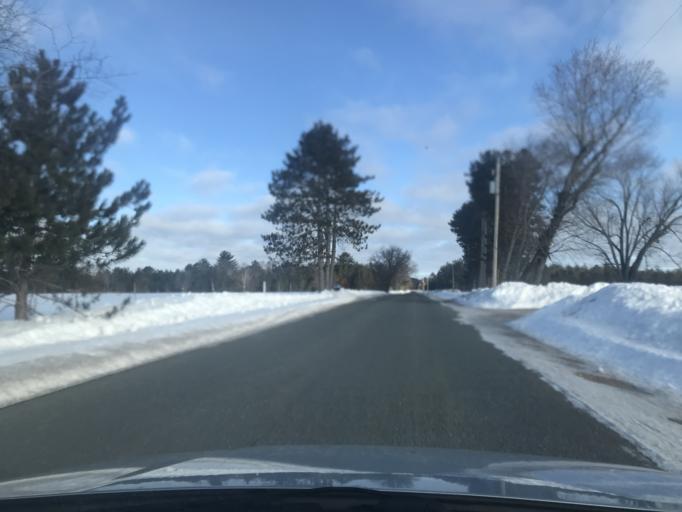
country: US
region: Wisconsin
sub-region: Marinette County
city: Niagara
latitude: 45.6178
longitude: -87.9769
